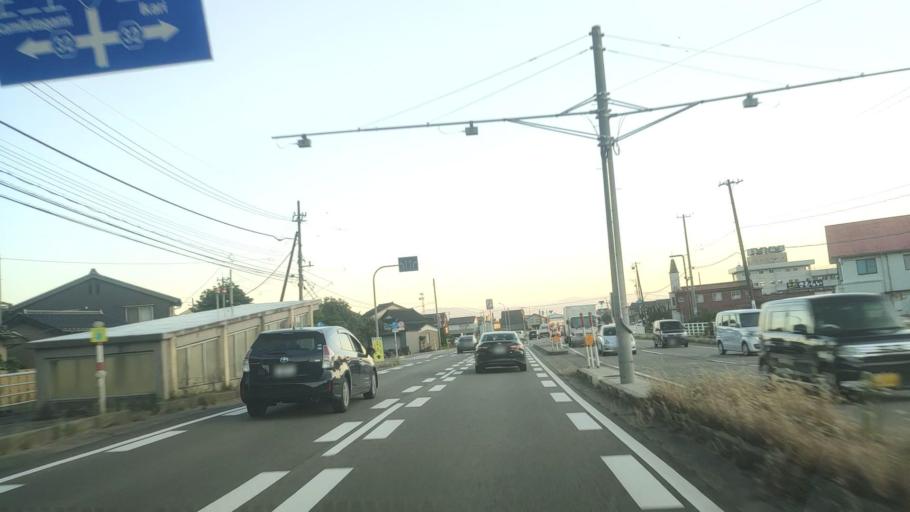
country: JP
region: Toyama
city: Takaoka
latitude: 36.7799
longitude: 137.0002
